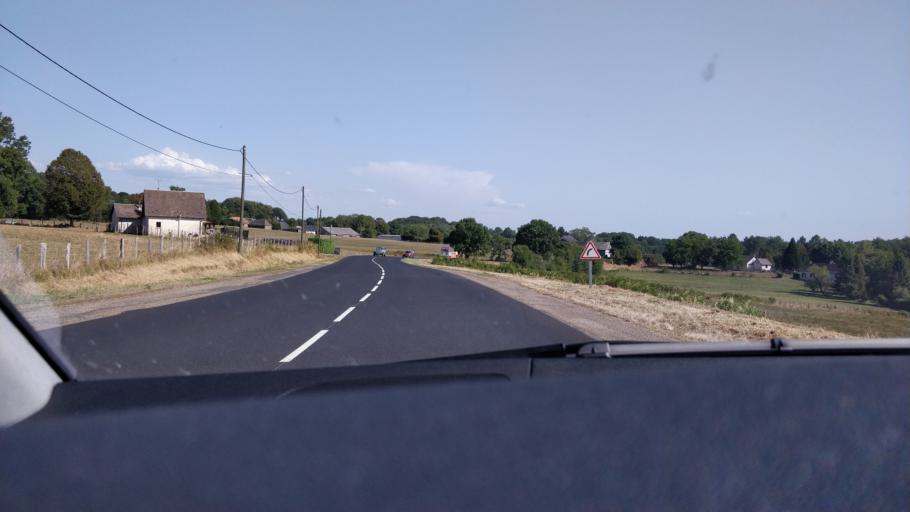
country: FR
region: Limousin
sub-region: Departement de la Correze
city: Uzerche
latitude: 45.4745
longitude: 1.5376
